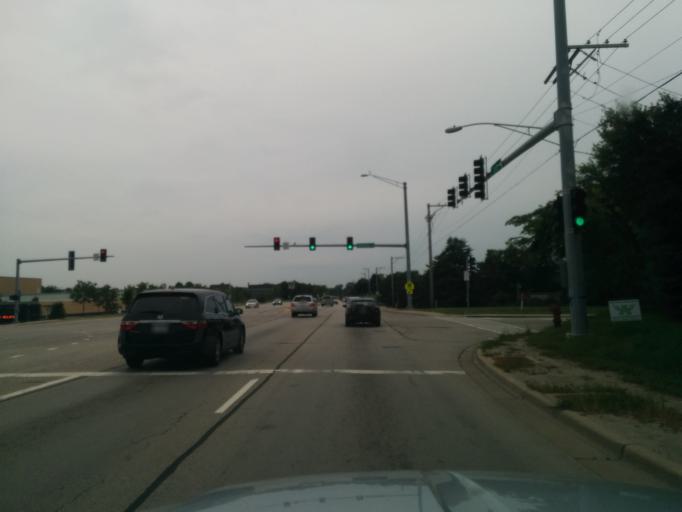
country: US
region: Illinois
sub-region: DuPage County
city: Warrenville
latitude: 41.7927
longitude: -88.2411
